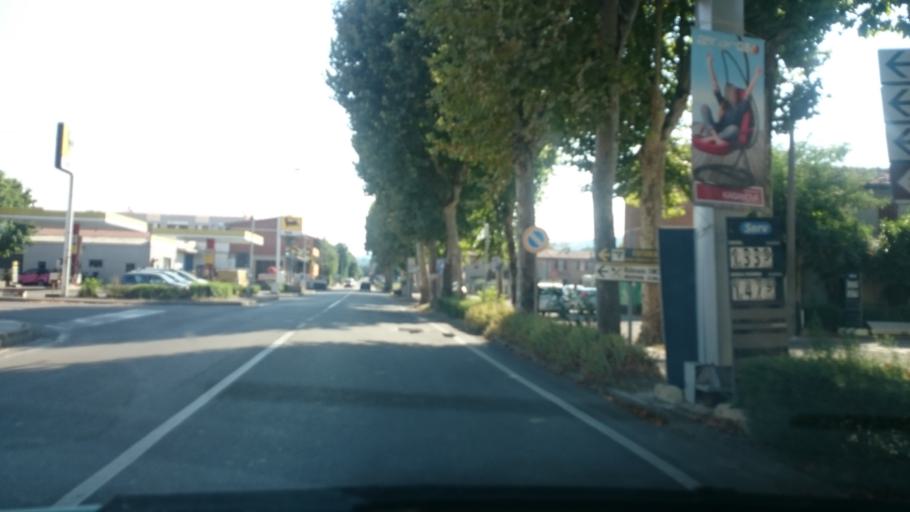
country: IT
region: Emilia-Romagna
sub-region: Provincia di Reggio Emilia
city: Scandiano
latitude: 44.5992
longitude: 10.6843
